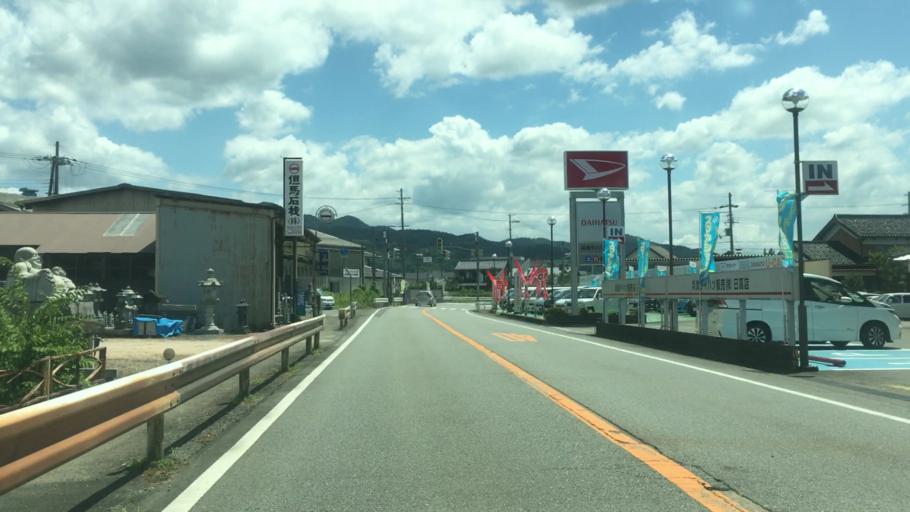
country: JP
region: Hyogo
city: Toyooka
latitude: 35.4899
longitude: 134.7999
